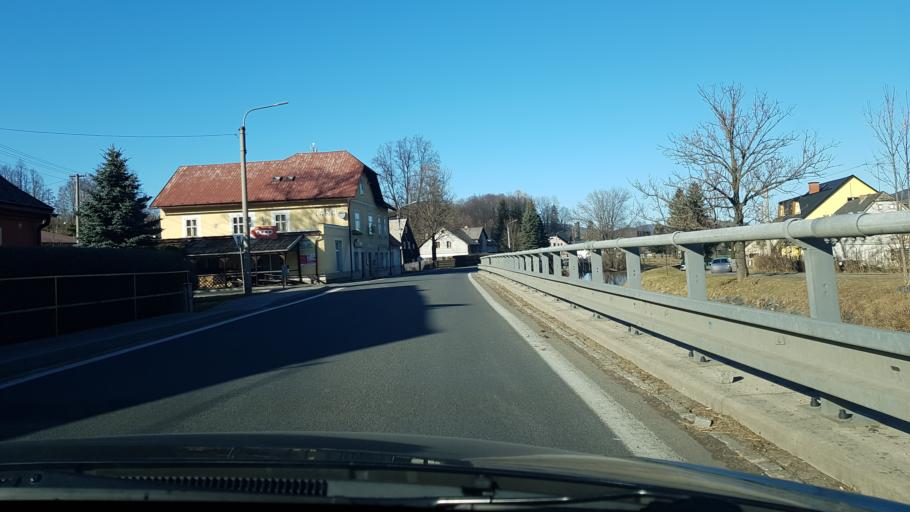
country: CZ
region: Olomoucky
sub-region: Okres Jesenik
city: Jesenik
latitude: 50.1964
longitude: 17.1933
